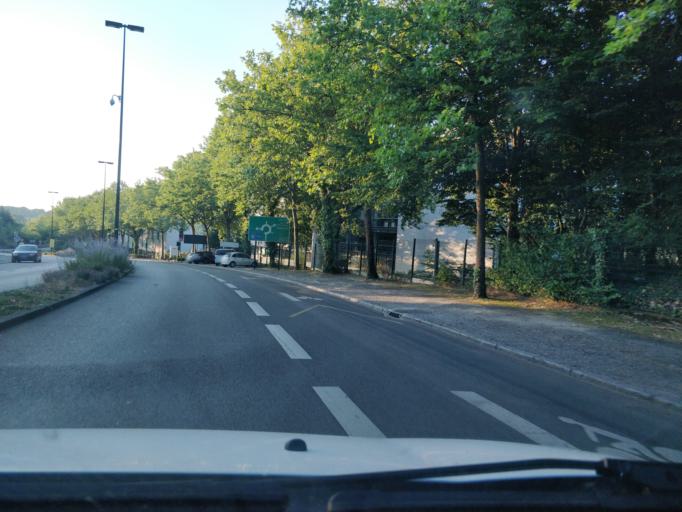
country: FR
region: Pays de la Loire
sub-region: Departement de la Loire-Atlantique
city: La Chapelle-sur-Erdre
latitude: 47.2601
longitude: -1.5599
